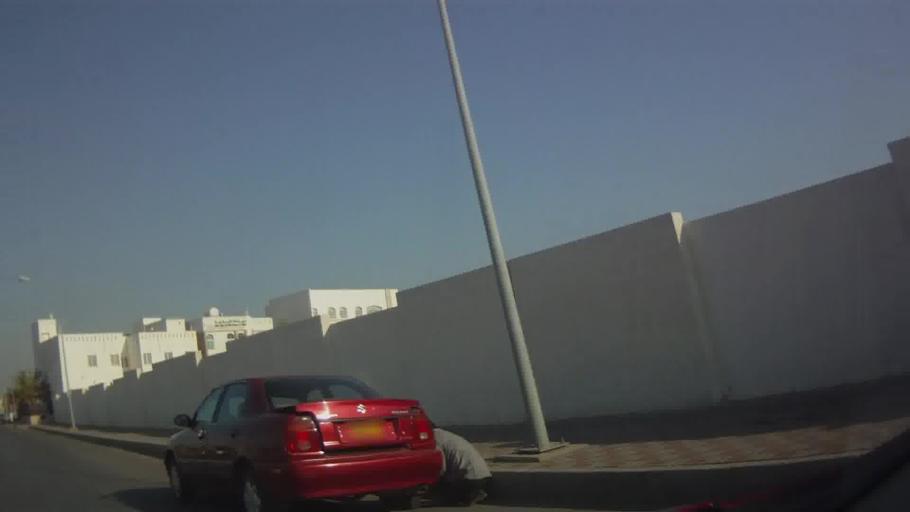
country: OM
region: Muhafazat Masqat
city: Bawshar
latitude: 23.5878
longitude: 58.4212
